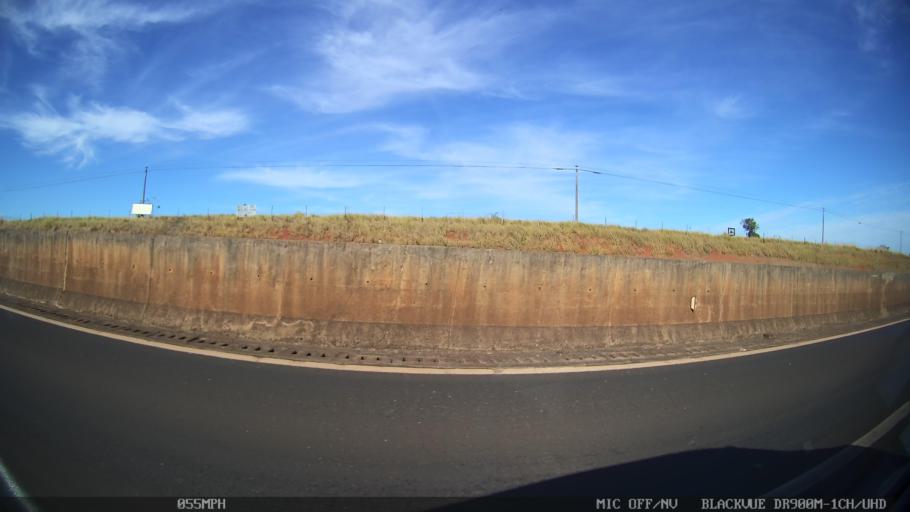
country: BR
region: Sao Paulo
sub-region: Sao Jose Do Rio Preto
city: Sao Jose do Rio Preto
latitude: -20.7467
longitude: -49.3398
